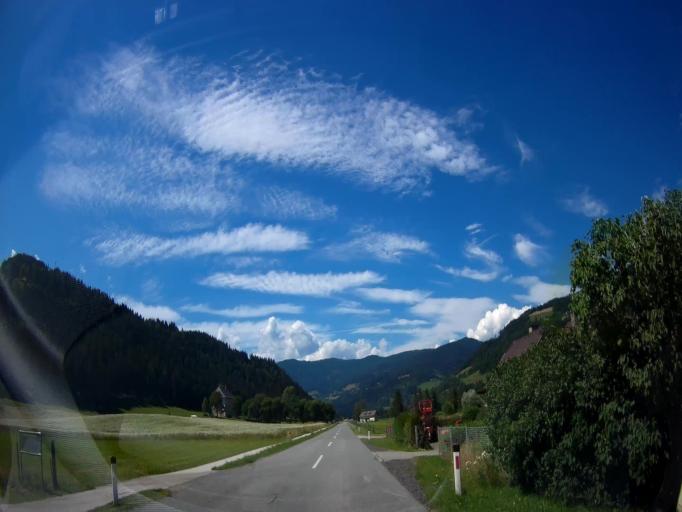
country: AT
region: Carinthia
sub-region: Politischer Bezirk Sankt Veit an der Glan
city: Glodnitz
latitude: 46.8778
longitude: 14.1162
